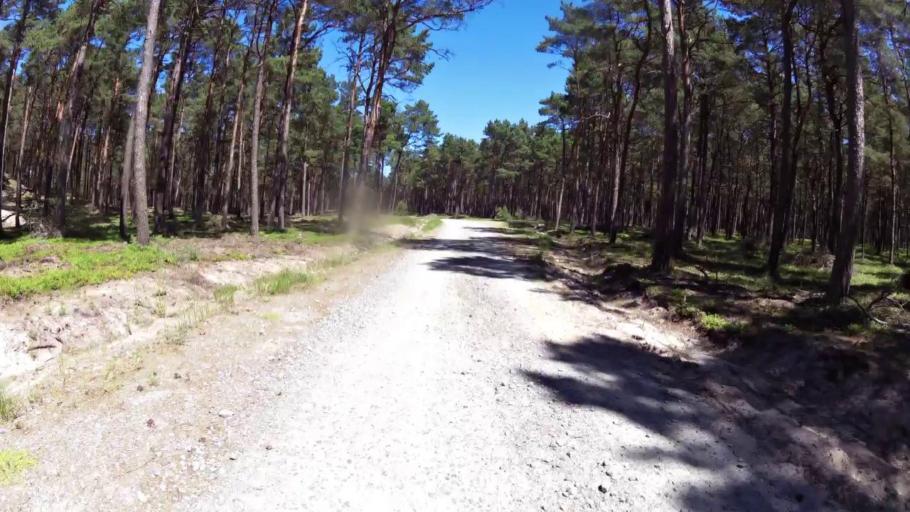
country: PL
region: West Pomeranian Voivodeship
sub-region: Powiat gryficki
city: Trzebiatow
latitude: 54.1097
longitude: 15.1961
